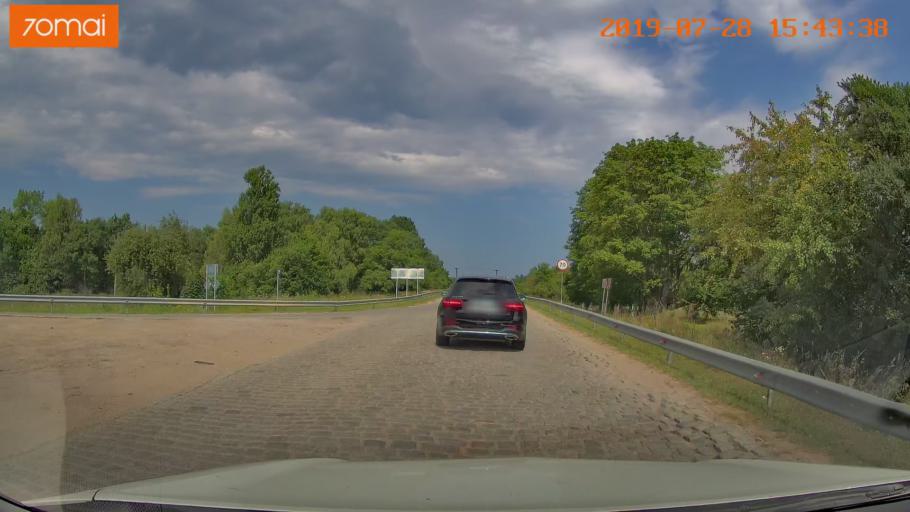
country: RU
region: Kaliningrad
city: Donskoye
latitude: 54.9379
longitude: 20.0261
